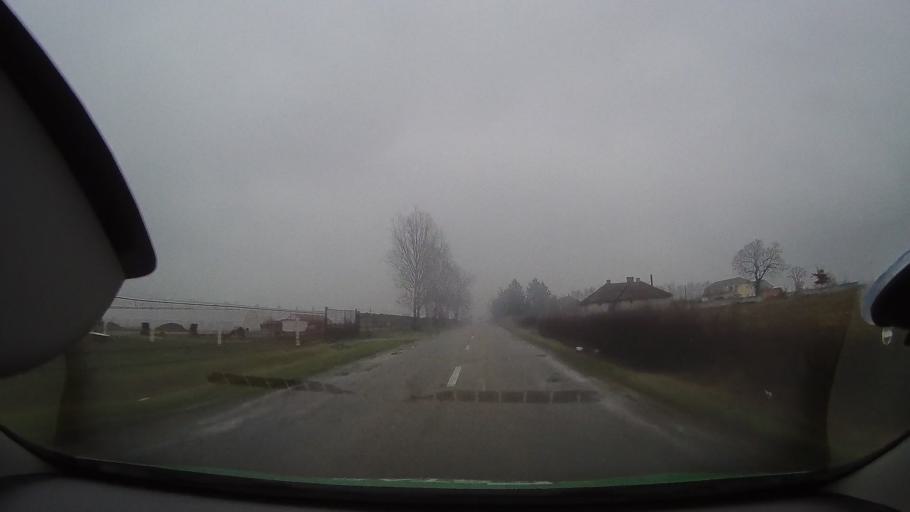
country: RO
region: Bihor
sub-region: Comuna Tinca
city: Tinca
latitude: 46.7713
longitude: 21.9049
